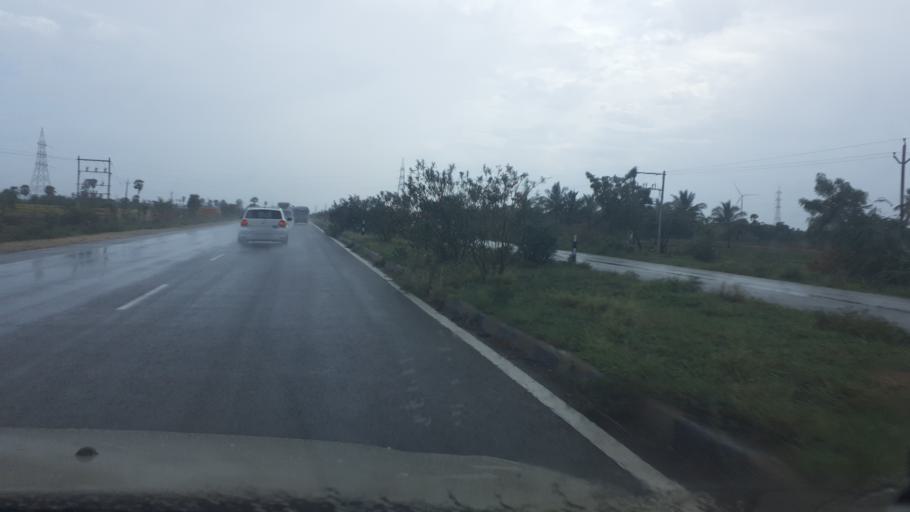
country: IN
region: Tamil Nadu
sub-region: Thoothukkudi
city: Kayattar
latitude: 8.9222
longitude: 77.7657
